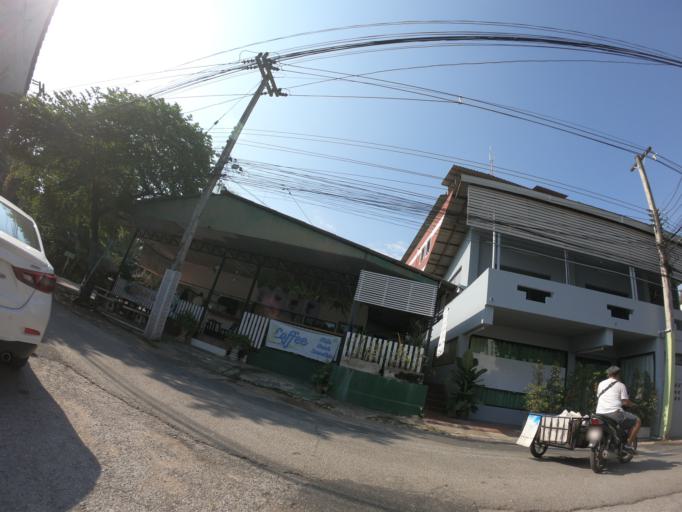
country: TH
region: Chiang Mai
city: Chiang Mai
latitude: 18.7884
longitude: 98.9568
